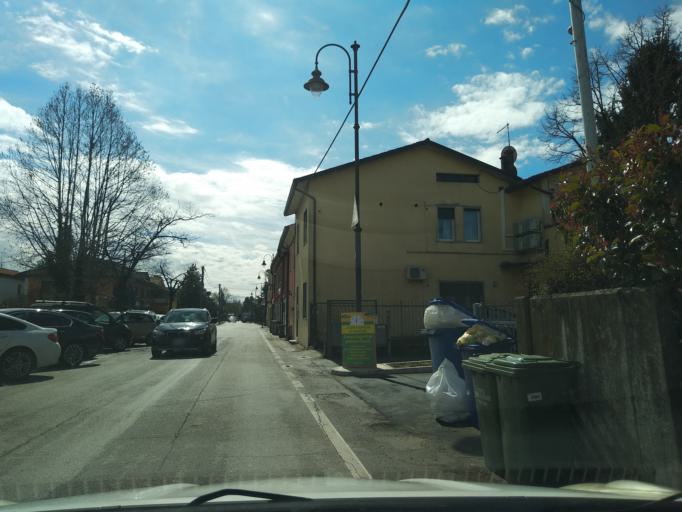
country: IT
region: Veneto
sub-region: Provincia di Vicenza
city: Bolzano Vicentino
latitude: 45.6017
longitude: 11.6141
